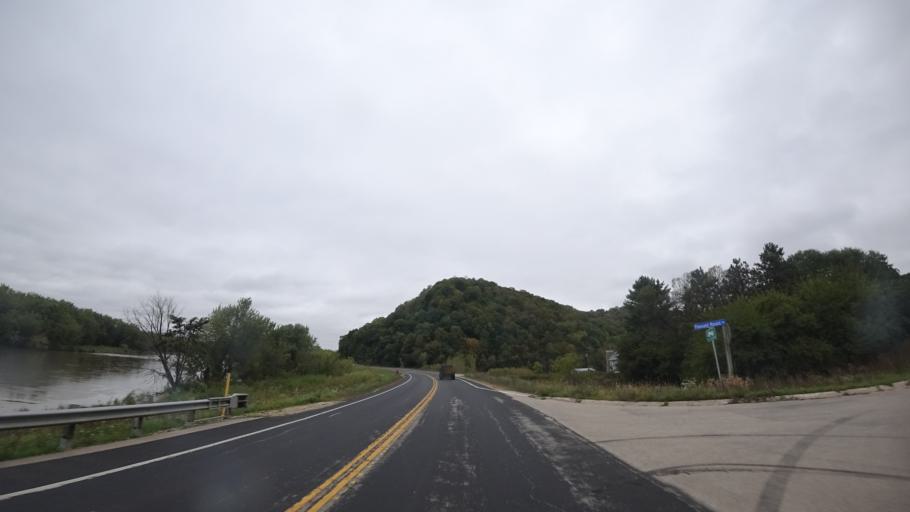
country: US
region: Wisconsin
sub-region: Grant County
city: Boscobel
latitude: 43.1379
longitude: -90.7409
